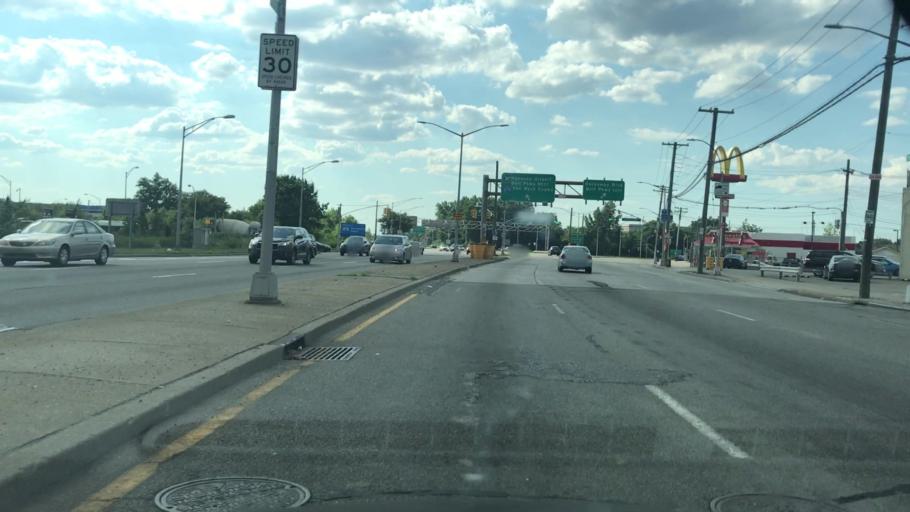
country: US
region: New York
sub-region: Nassau County
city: Inwood
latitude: 40.6591
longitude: -73.7729
